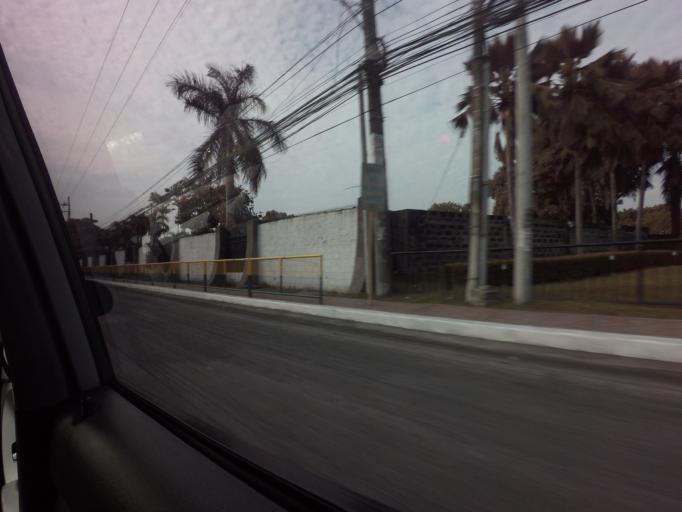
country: PH
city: Sambayanihan People's Village
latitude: 14.4610
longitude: 121.0259
